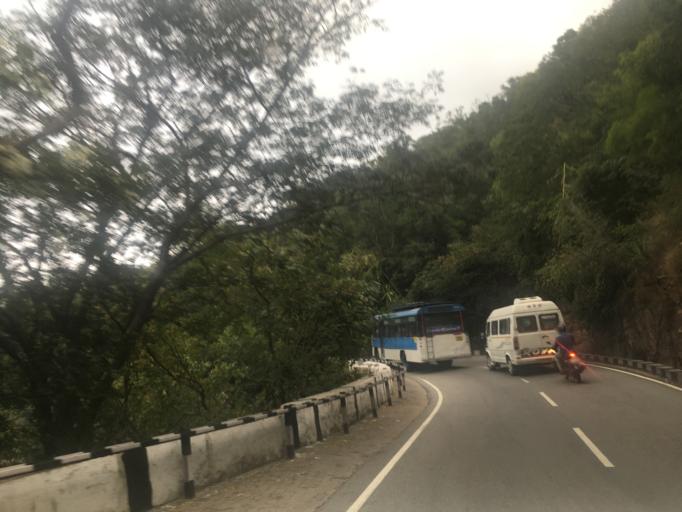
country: IN
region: Andhra Pradesh
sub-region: Chittoor
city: Tirumala
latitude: 13.6638
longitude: 79.3508
